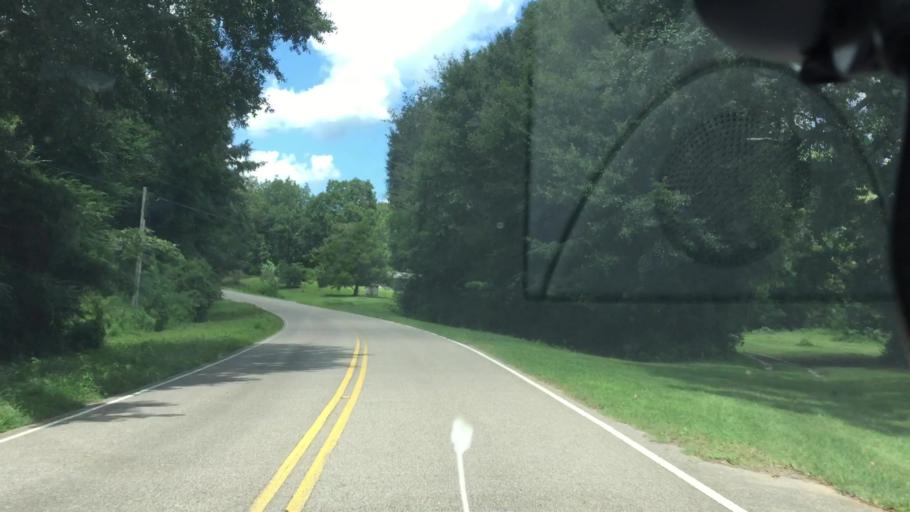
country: US
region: Alabama
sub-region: Coffee County
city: Enterprise
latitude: 31.3986
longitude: -85.8312
